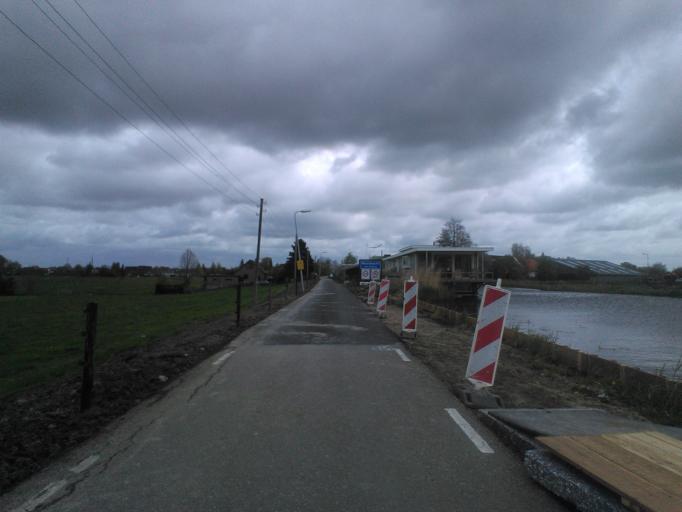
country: NL
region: South Holland
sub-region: Gemeente Gouda
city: Bloemendaal
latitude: 51.9797
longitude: 4.6535
